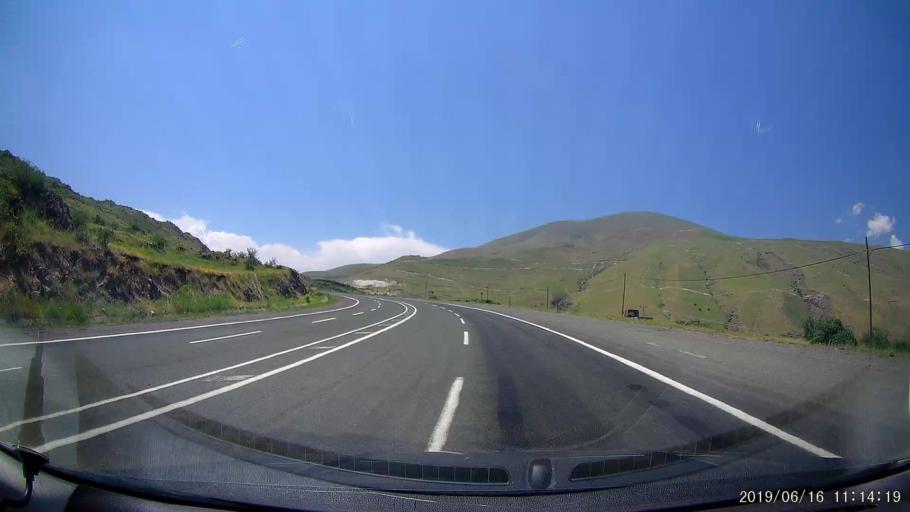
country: TR
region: Igdir
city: Igdir
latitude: 39.7810
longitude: 44.1431
